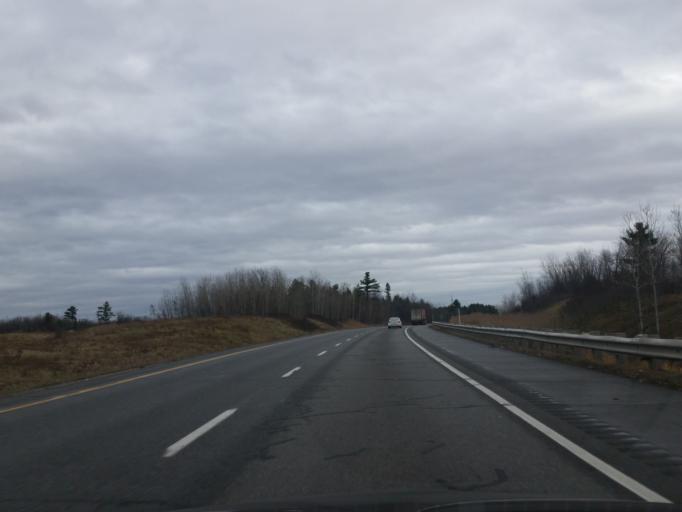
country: CA
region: Ontario
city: Clarence-Rockland
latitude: 45.5400
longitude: -75.4806
